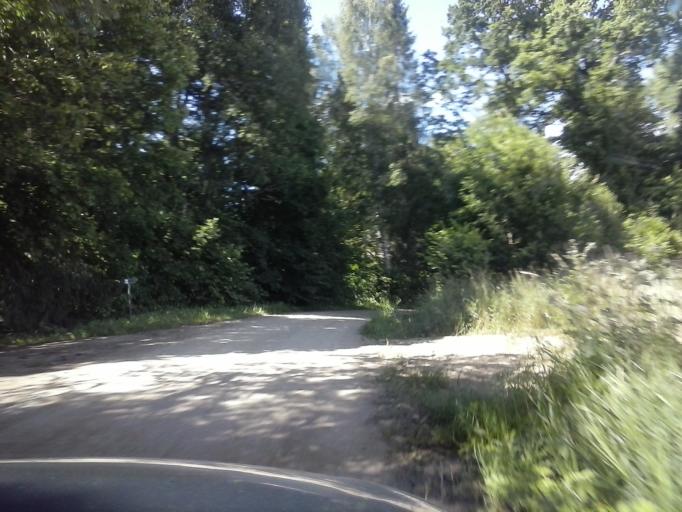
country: LV
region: Apes Novads
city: Ape
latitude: 57.5713
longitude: 26.6685
